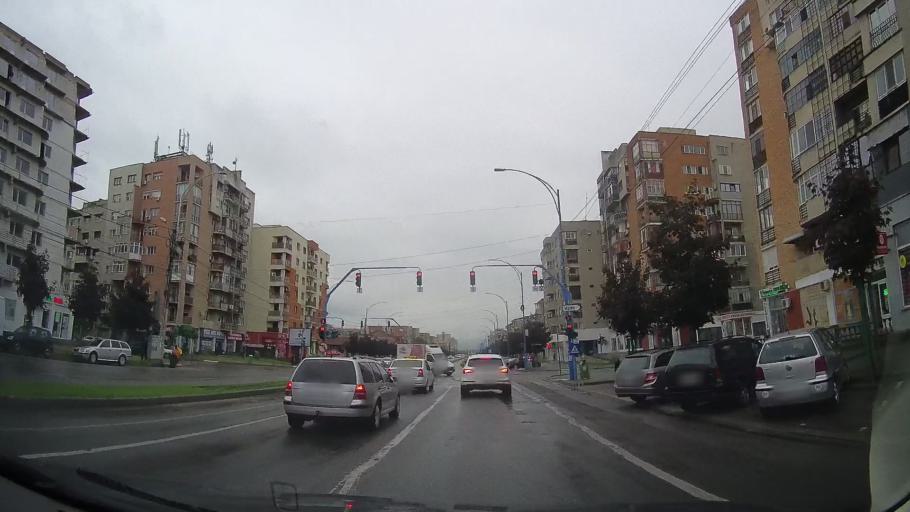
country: RO
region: Mehedinti
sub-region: Municipiul Drobeta-Turnu Severin
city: Drobeta-Turnu Severin
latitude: 44.6326
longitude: 22.6656
